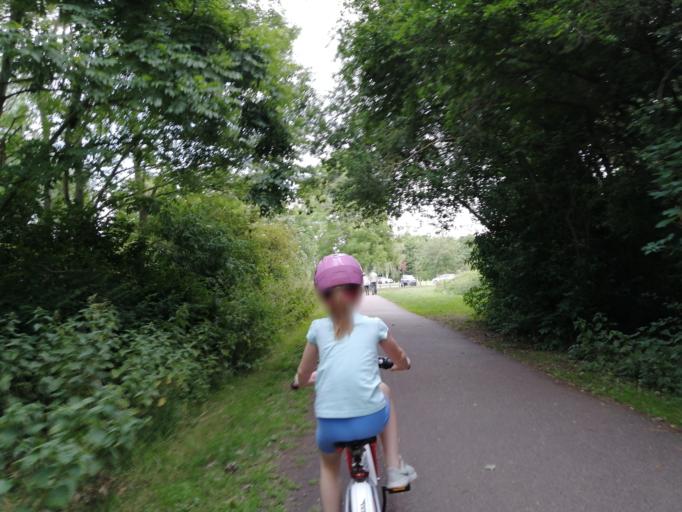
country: GB
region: England
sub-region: Peterborough
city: Peterborough
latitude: 52.5591
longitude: -0.2839
